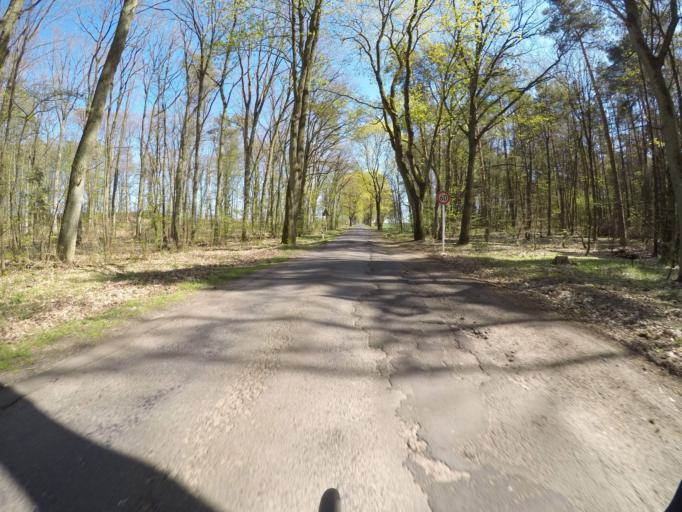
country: DE
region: Brandenburg
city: Strausberg
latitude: 52.6200
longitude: 13.8416
